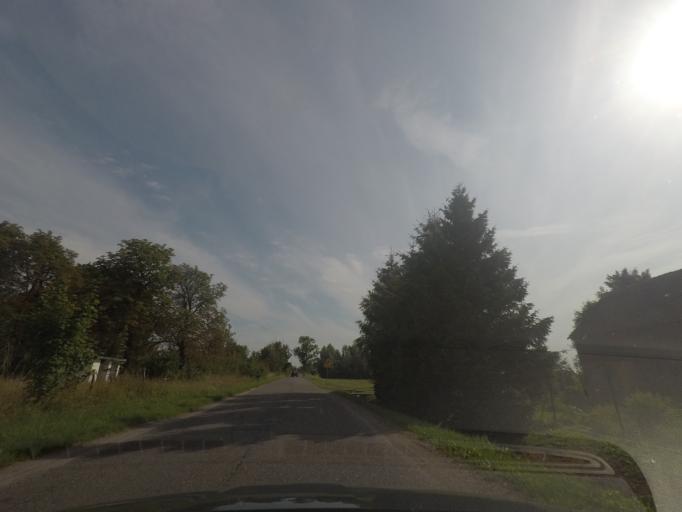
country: PL
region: Pomeranian Voivodeship
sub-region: Powiat slupski
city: Smoldzino
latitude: 54.6270
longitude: 17.2427
